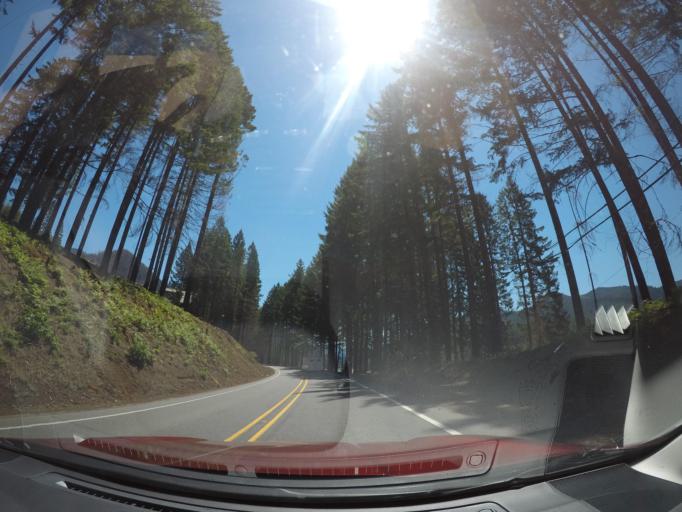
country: US
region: Oregon
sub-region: Linn County
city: Mill City
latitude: 44.7300
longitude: -122.1474
